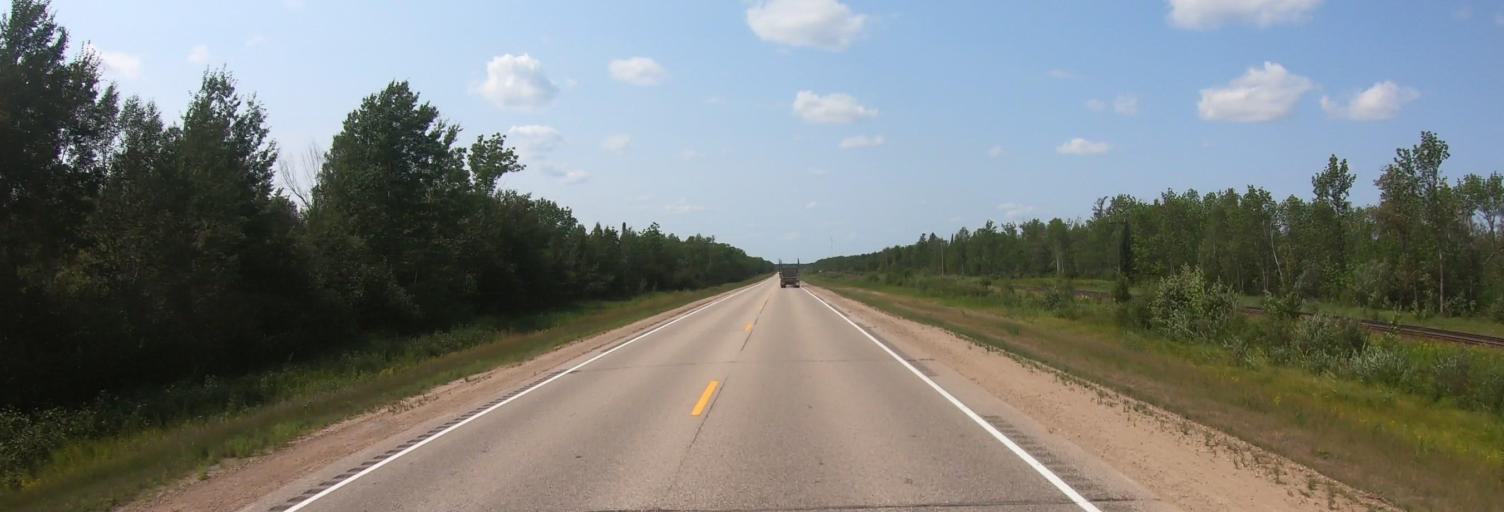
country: US
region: Minnesota
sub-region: Roseau County
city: Warroad
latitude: 48.7912
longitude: -95.0580
